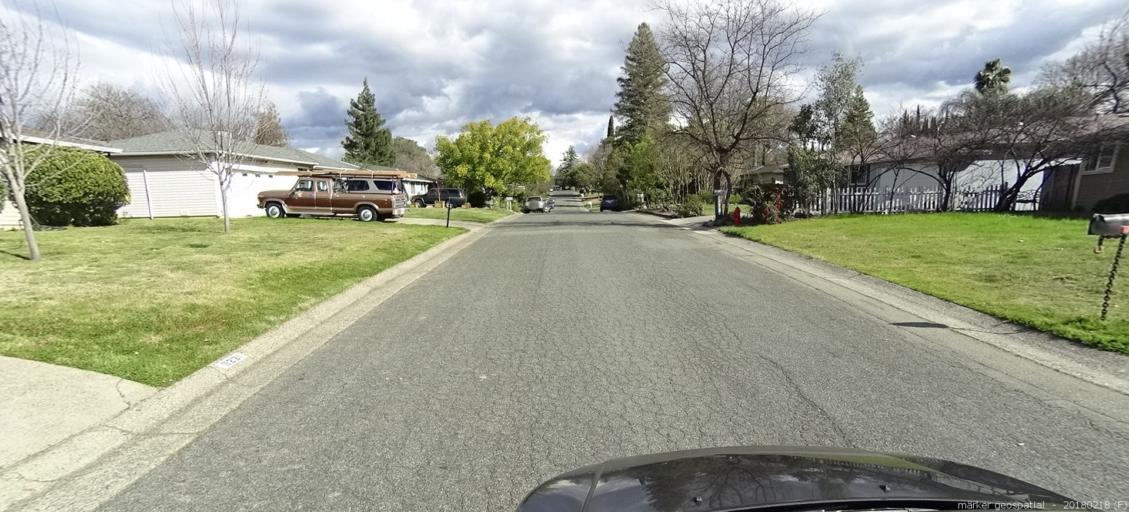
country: US
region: California
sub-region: Sacramento County
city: Orangevale
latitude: 38.6770
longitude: -121.2099
